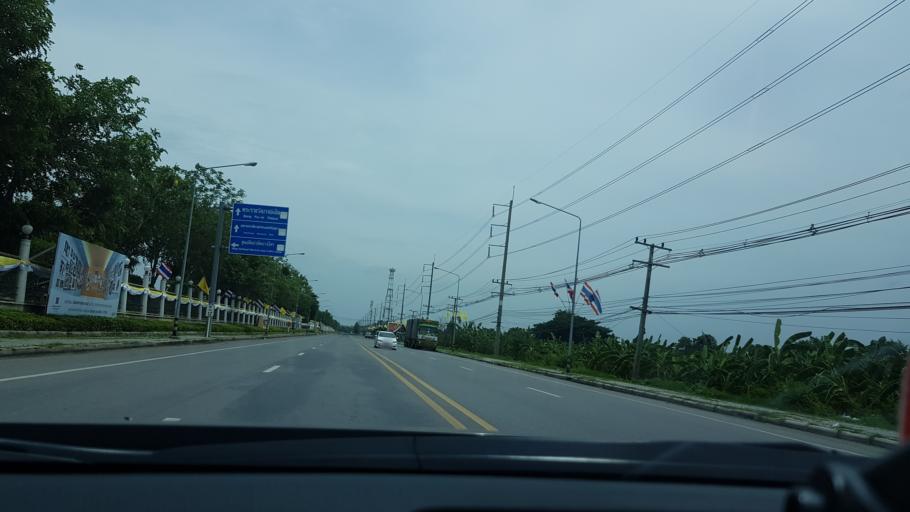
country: TH
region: Pathum Thani
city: Sam Khok
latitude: 14.1482
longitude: 100.5242
